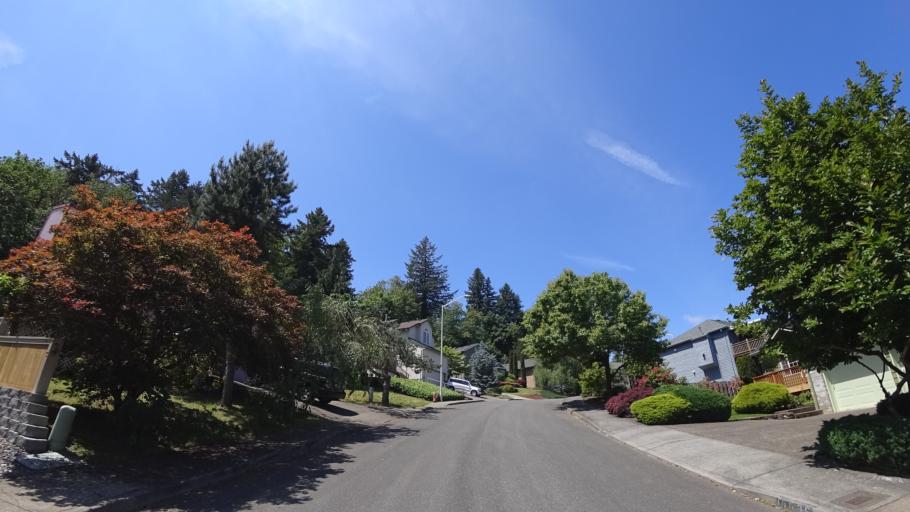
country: US
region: Oregon
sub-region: Clackamas County
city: Happy Valley
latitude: 45.4894
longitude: -122.4914
